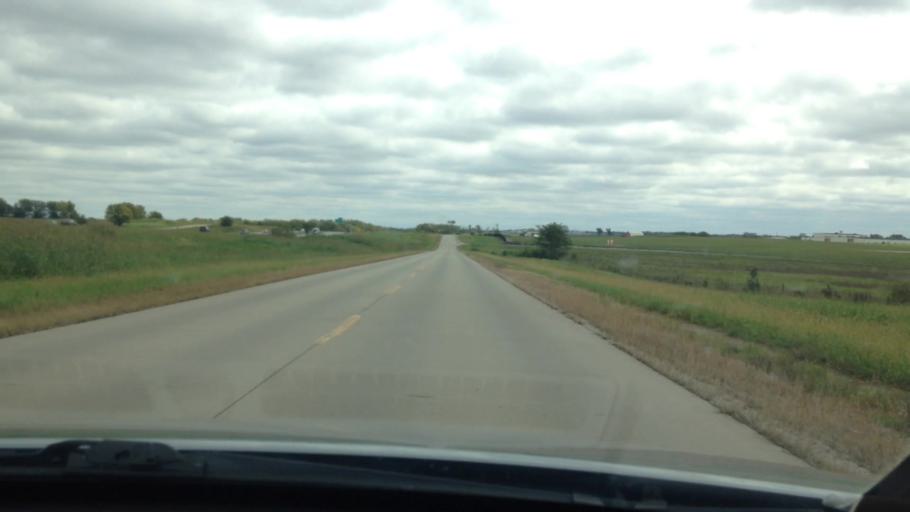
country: US
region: Missouri
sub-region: Platte County
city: Platte City
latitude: 39.3344
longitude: -94.7236
